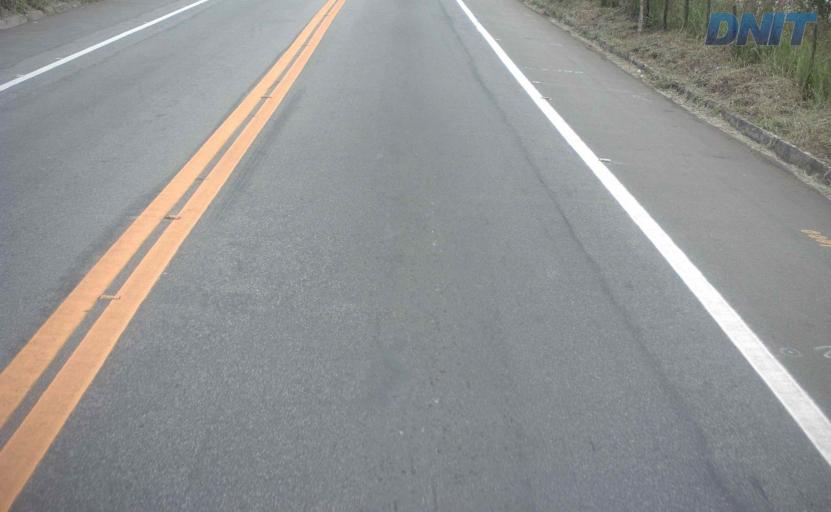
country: BR
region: Minas Gerais
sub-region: Timoteo
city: Timoteo
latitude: -19.6083
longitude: -42.7639
